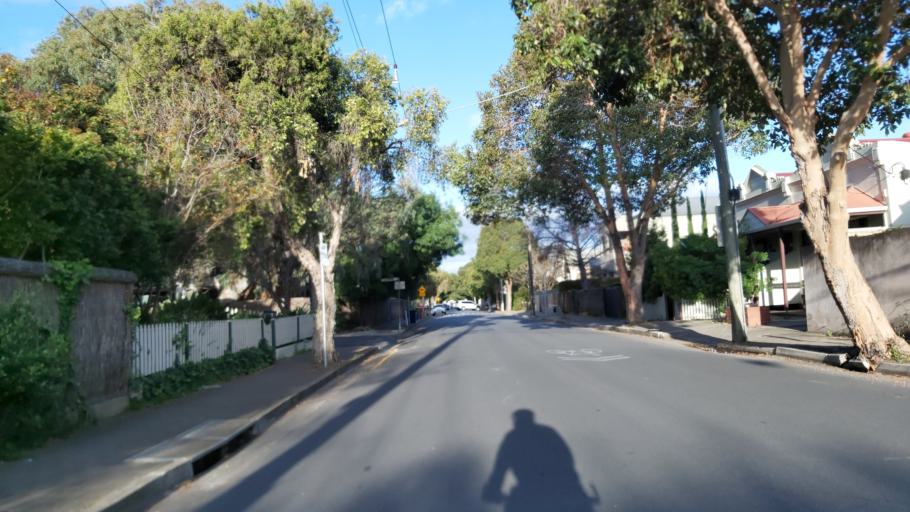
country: AU
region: South Australia
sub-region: Unley
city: Unley
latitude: -34.9495
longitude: 138.5942
